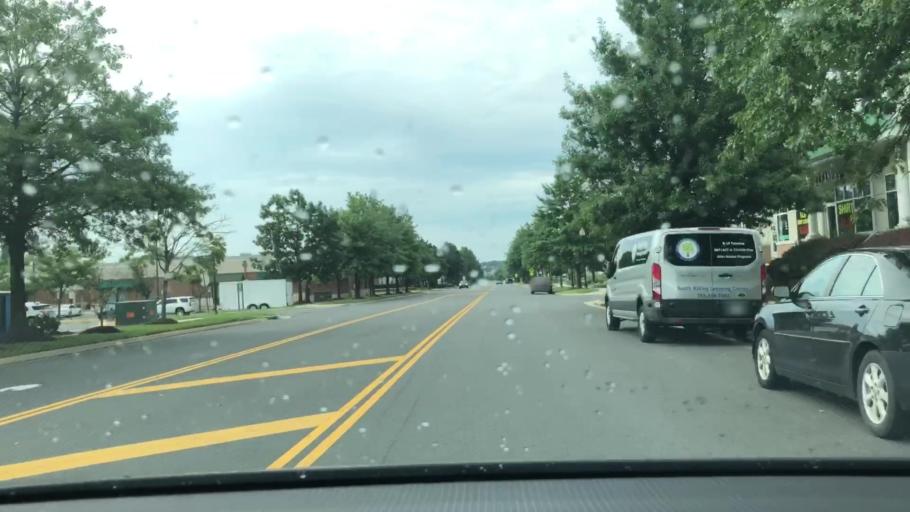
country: US
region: Virginia
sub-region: Loudoun County
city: South Riding
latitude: 38.9155
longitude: -77.5136
